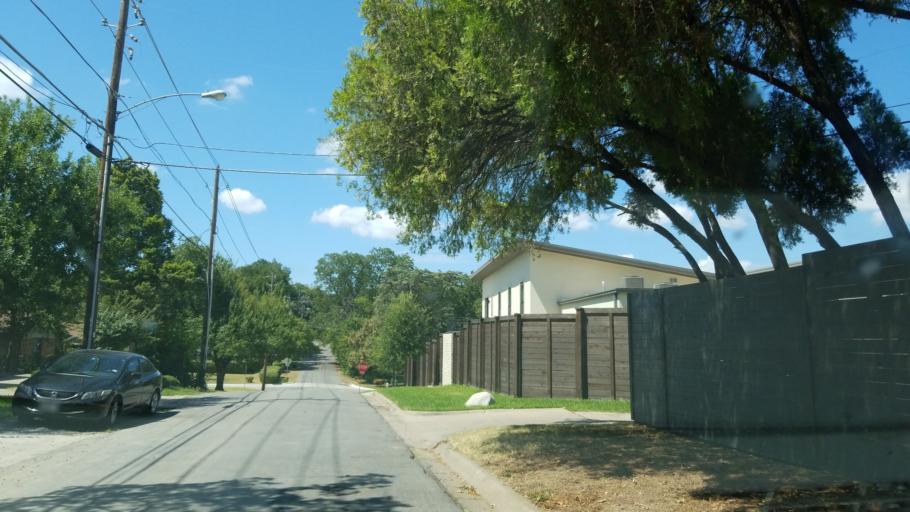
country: US
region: Texas
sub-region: Dallas County
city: Dallas
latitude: 32.7623
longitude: -96.8335
